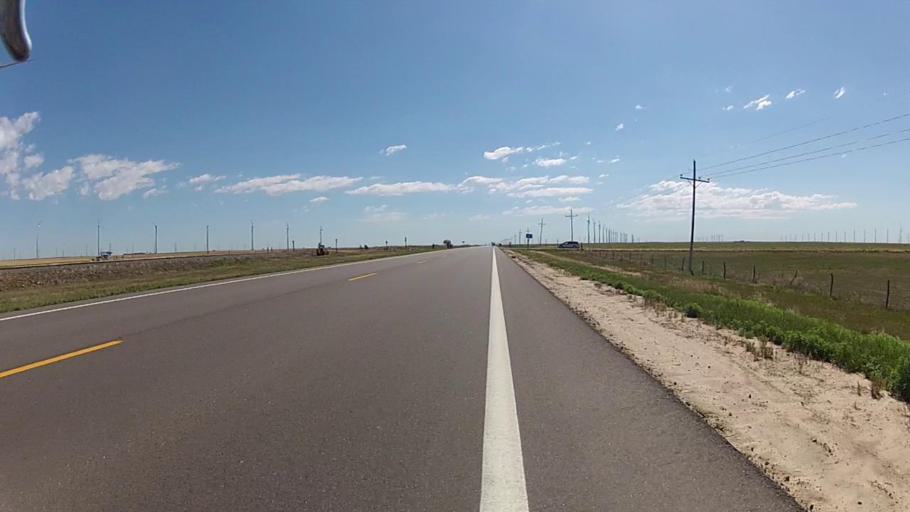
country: US
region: Kansas
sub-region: Gray County
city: Cimarron
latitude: 37.6117
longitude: -100.3986
